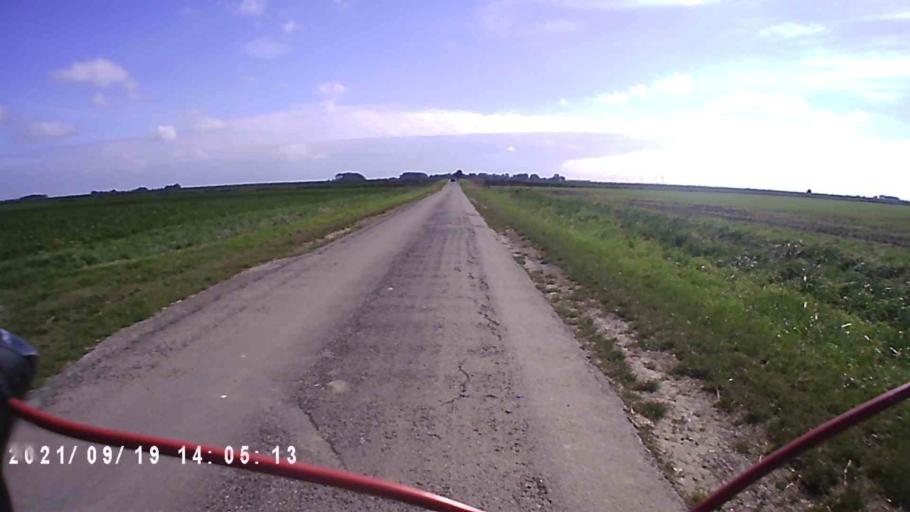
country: NL
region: Groningen
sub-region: Gemeente  Oldambt
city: Winschoten
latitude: 53.1446
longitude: 7.1216
